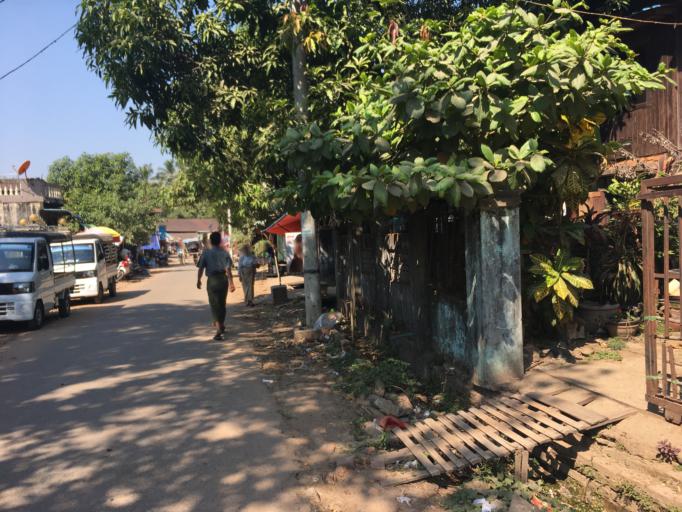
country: MM
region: Mon
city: Mawlamyine
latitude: 16.4346
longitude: 97.7049
